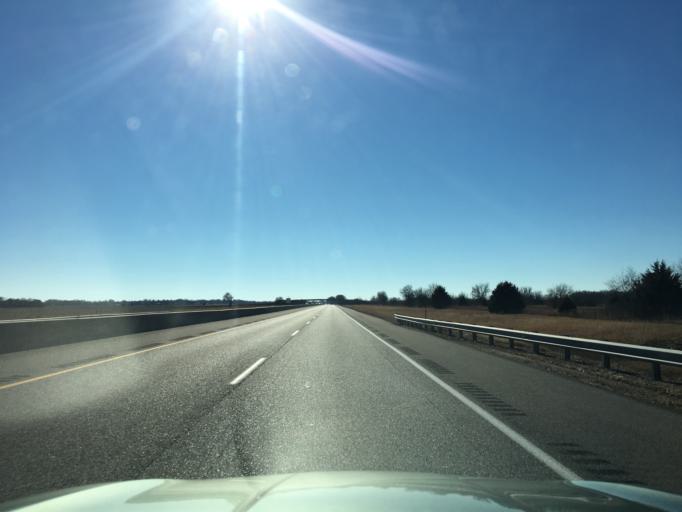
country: US
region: Kansas
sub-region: Sumner County
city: Belle Plaine
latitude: 37.4571
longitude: -97.3225
